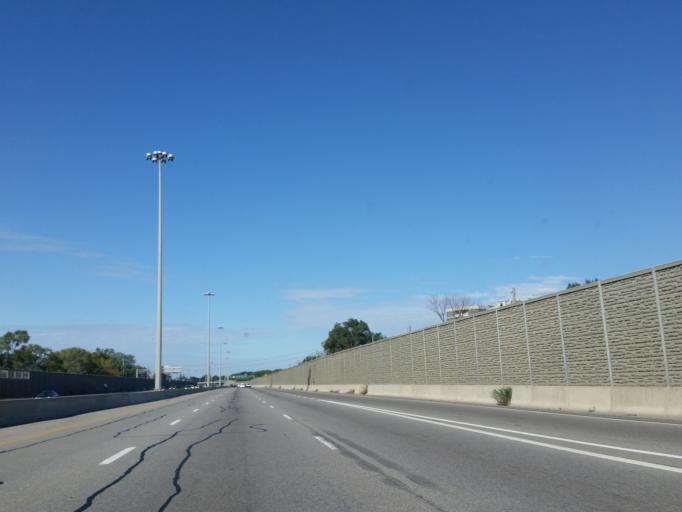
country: CA
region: Ontario
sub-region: Regional Municipality of Niagara
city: St. Catharines
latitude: 43.1779
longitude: -79.2547
